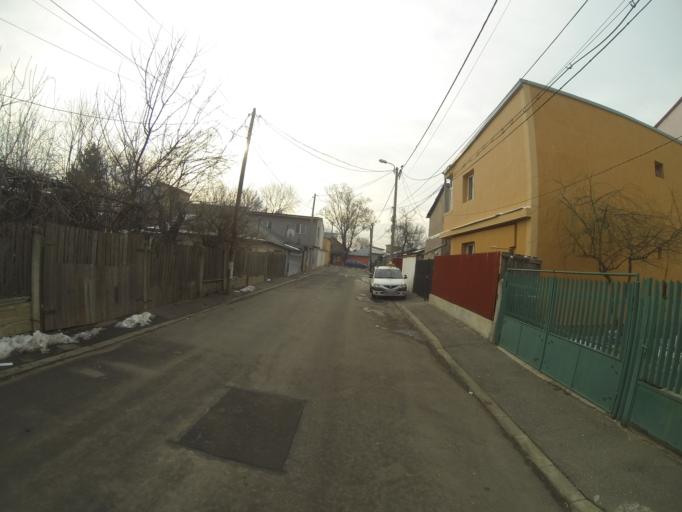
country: RO
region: Bucuresti
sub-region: Municipiul Bucuresti
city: Bucuresti
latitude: 44.3968
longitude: 26.0757
